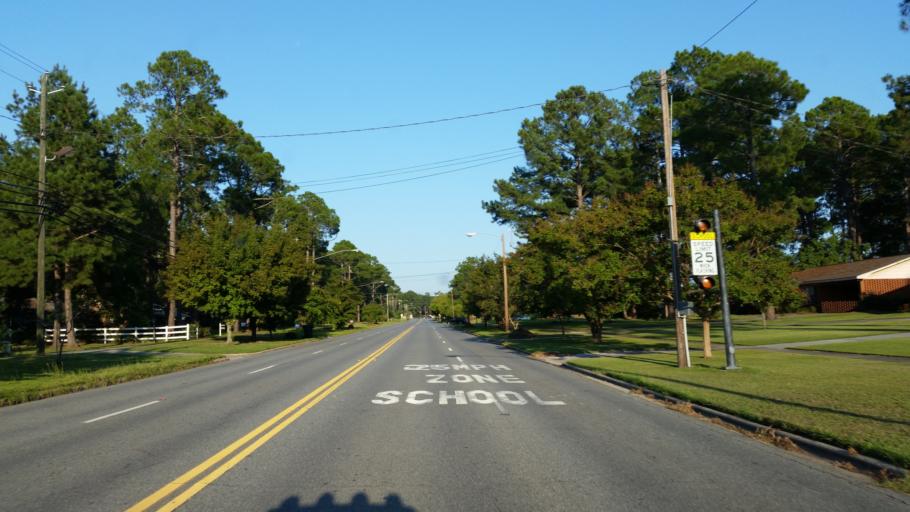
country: US
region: Georgia
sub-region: Tift County
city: Tifton
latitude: 31.4633
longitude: -83.5249
